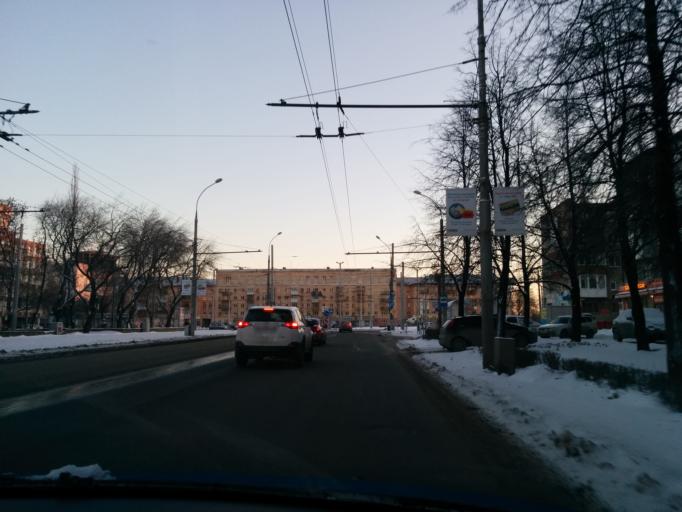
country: RU
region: Perm
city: Perm
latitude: 57.9982
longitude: 56.2609
